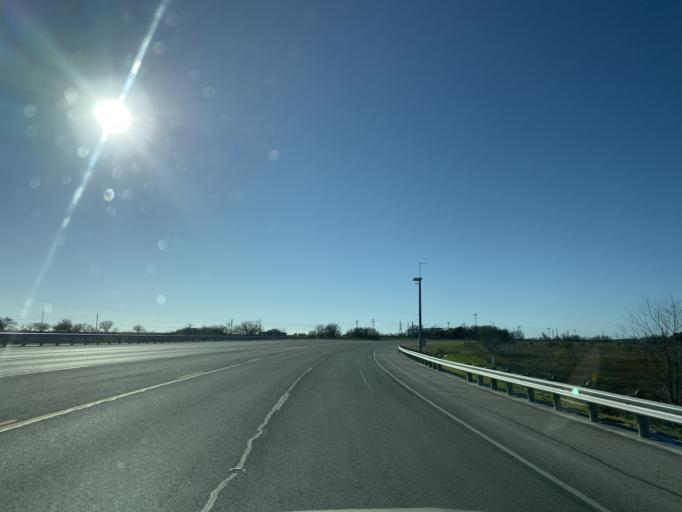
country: US
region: Texas
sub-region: Guadalupe County
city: Redwood
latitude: 29.8284
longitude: -97.9544
